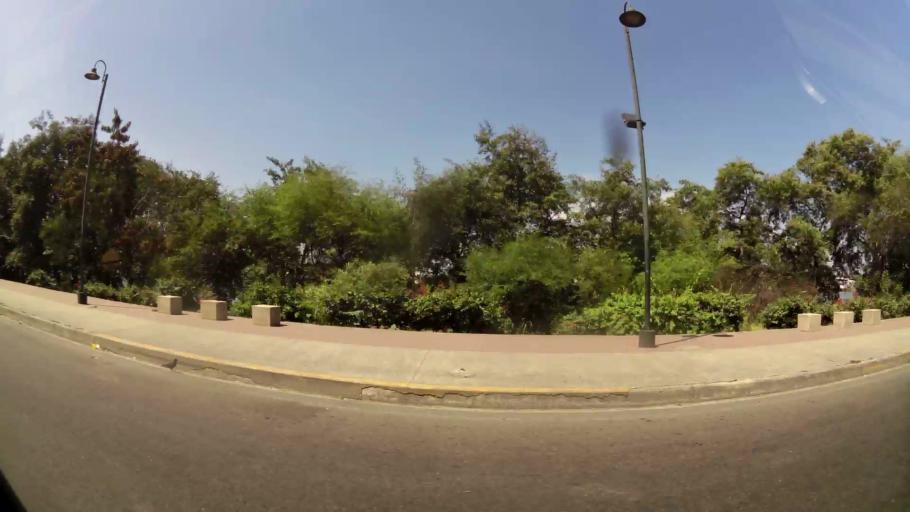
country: EC
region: Guayas
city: Guayaquil
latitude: -2.1922
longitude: -79.9341
